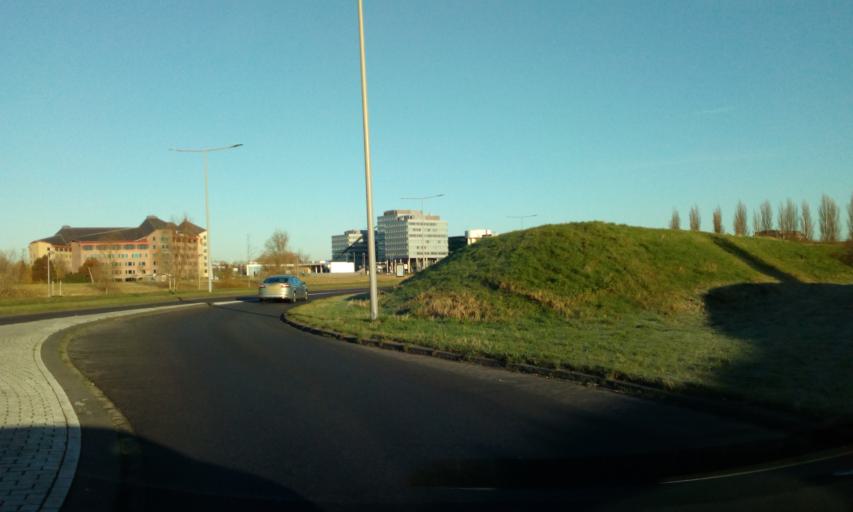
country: NL
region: South Holland
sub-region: Gemeente Den Haag
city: Ypenburg
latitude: 52.0678
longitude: 4.3994
